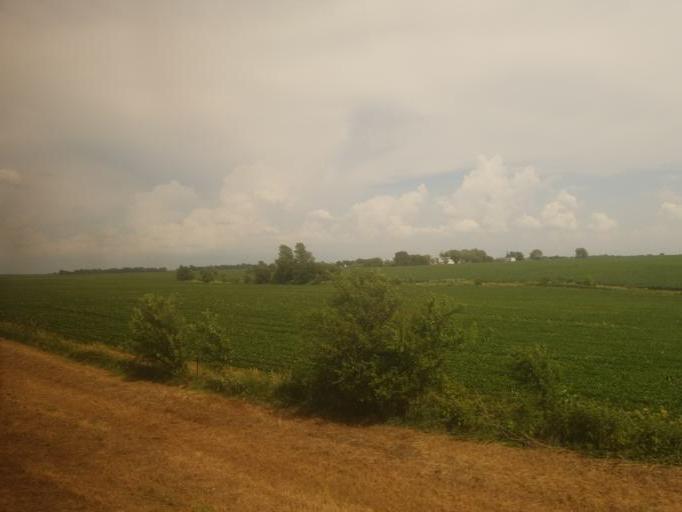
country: US
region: Illinois
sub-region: Knox County
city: Galesburg
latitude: 40.9078
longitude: -90.4310
